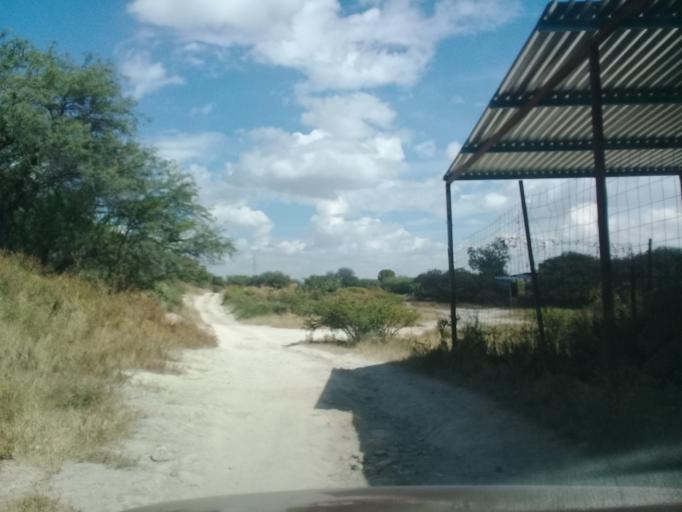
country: MX
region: Aguascalientes
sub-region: Aguascalientes
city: Penuelas (El Cienegal)
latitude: 21.7732
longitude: -102.3106
